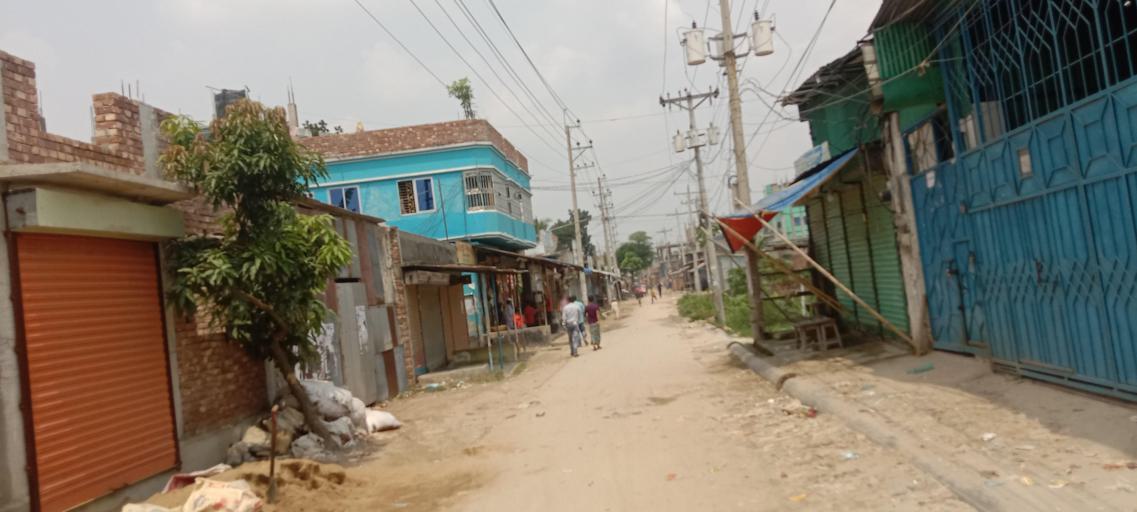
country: BD
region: Dhaka
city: Azimpur
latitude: 23.7059
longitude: 90.3549
